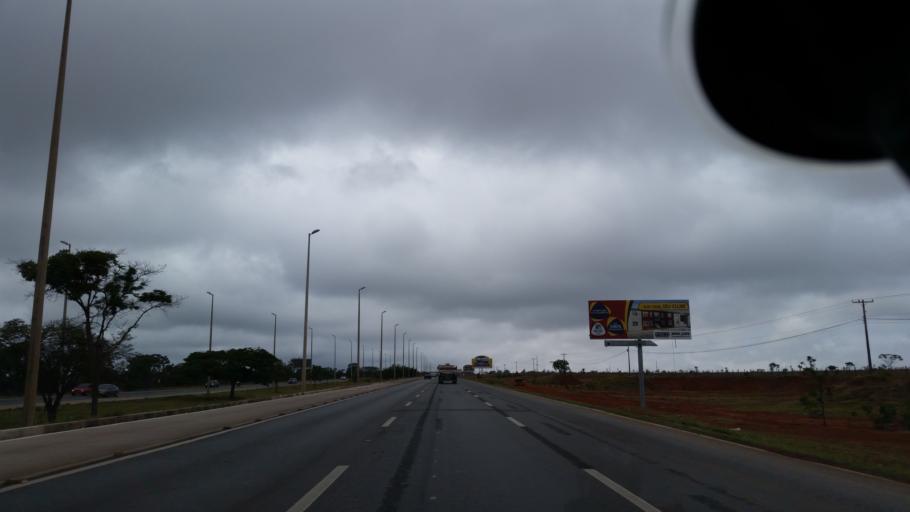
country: BR
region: Federal District
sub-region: Brasilia
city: Brasilia
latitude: -15.9624
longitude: -47.9929
